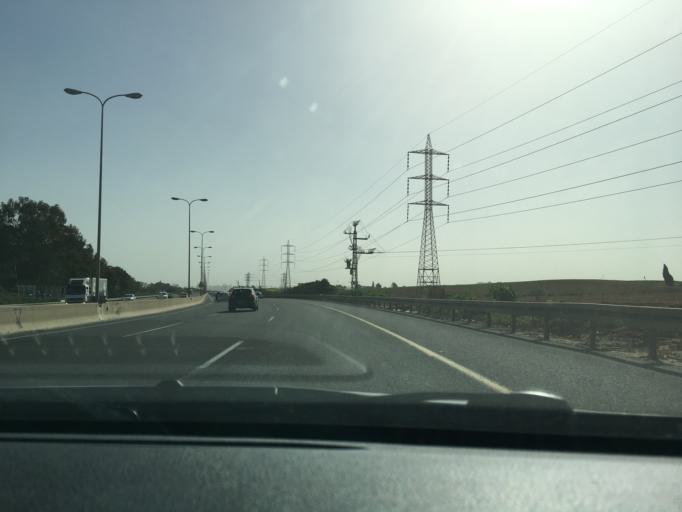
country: IL
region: Central District
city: Hod HaSharon
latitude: 32.1548
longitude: 34.8725
